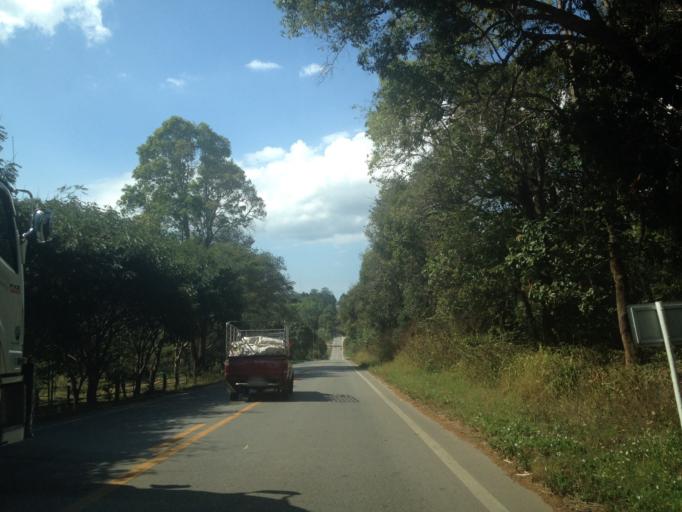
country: TH
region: Chiang Mai
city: Hot
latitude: 18.1455
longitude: 98.3613
